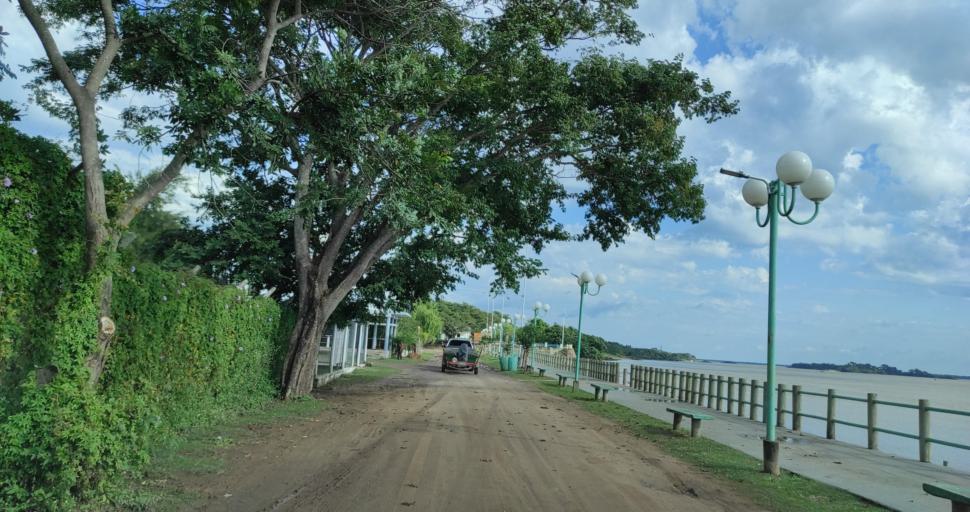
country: AR
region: Corrientes
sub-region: Departamento de Itati
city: Itati
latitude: -27.2665
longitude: -58.2459
